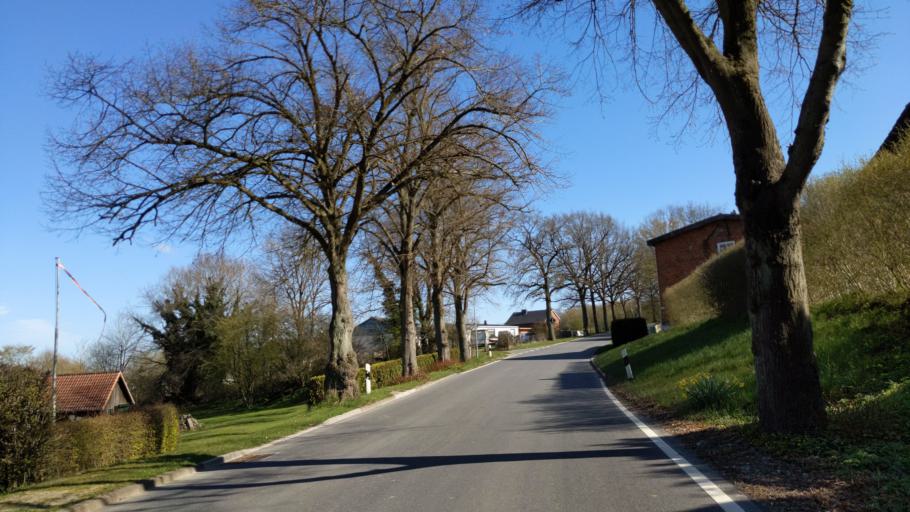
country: DE
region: Schleswig-Holstein
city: Eutin
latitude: 54.0901
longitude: 10.6181
